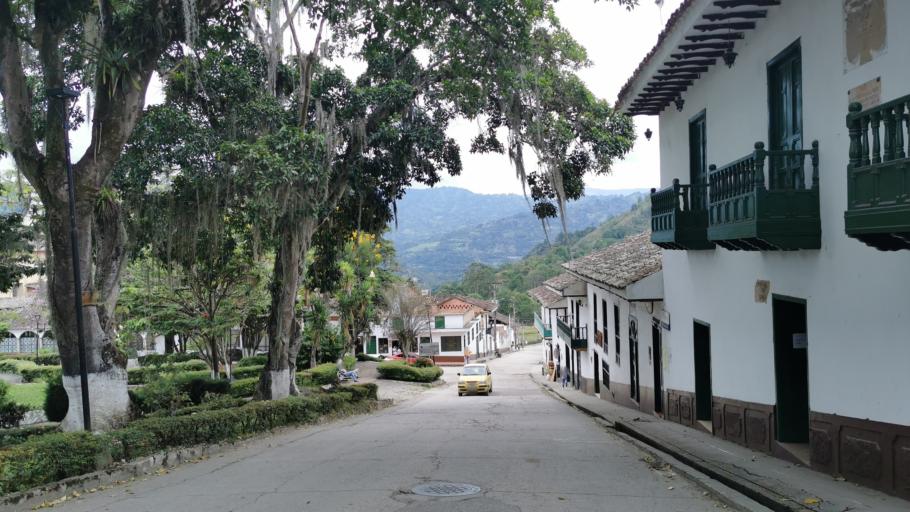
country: CO
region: Cundinamarca
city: Tenza
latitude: 5.0765
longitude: -73.4200
